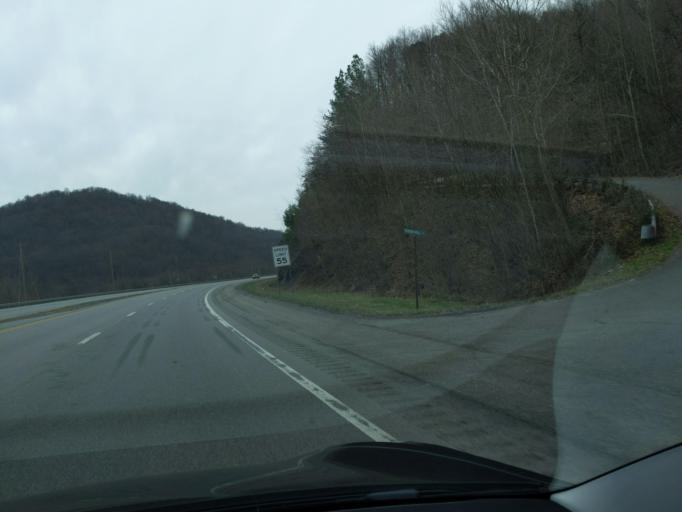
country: US
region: Kentucky
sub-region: Bell County
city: Pineville
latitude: 36.7896
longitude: -83.7450
